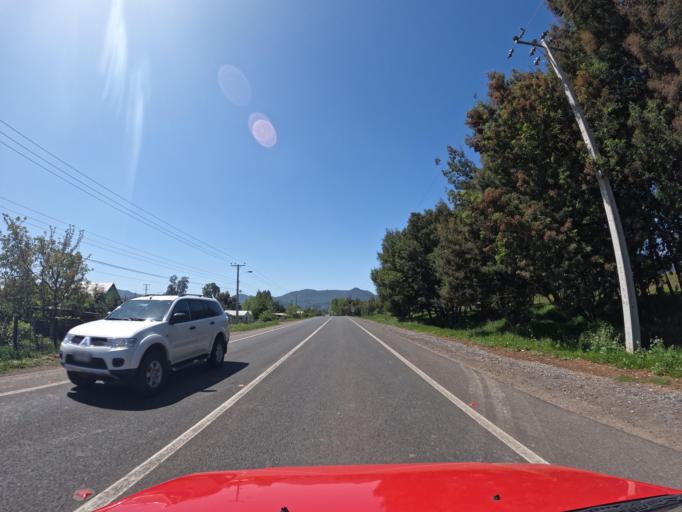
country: CL
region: Maule
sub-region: Provincia de Linares
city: Colbun
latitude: -35.7142
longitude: -71.4022
